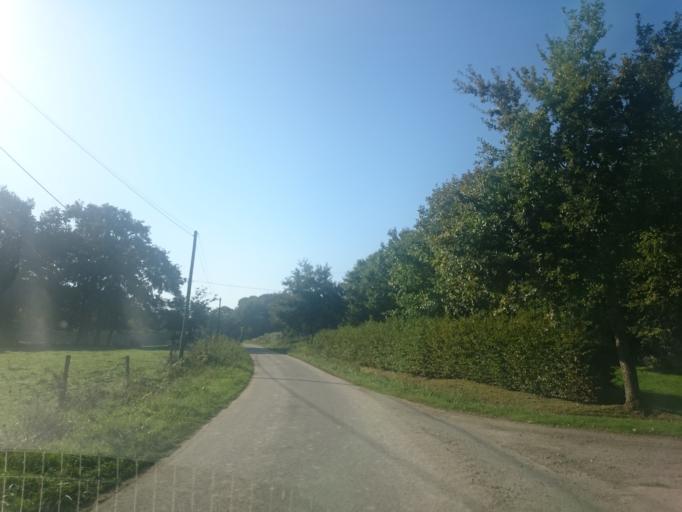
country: FR
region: Brittany
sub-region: Departement d'Ille-et-Vilaine
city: Chanteloup
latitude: 47.9394
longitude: -1.5891
